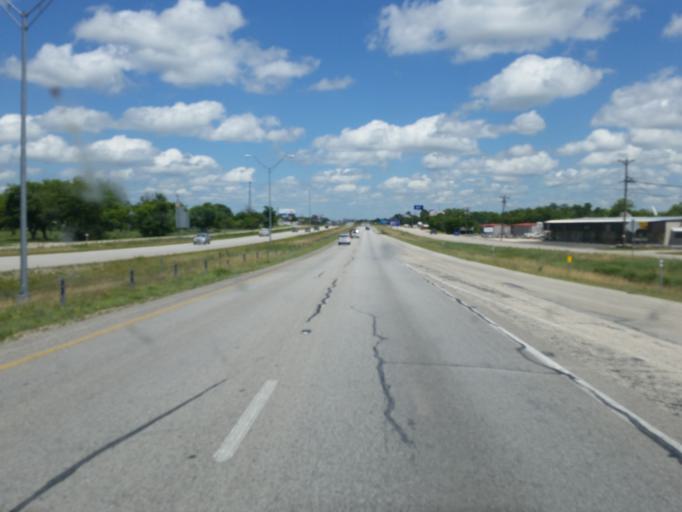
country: US
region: Texas
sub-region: Callahan County
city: Clyde
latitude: 32.4144
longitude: -99.5039
